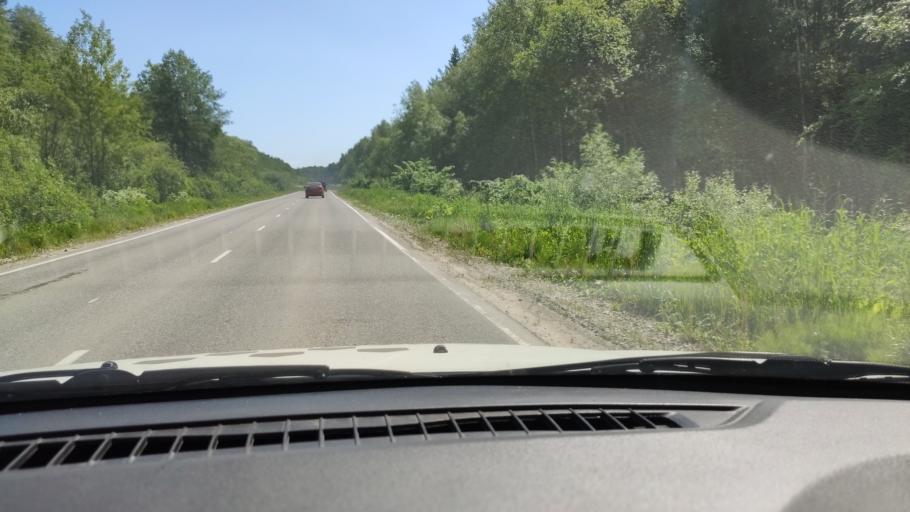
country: RU
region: Perm
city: Novyye Lyady
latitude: 58.0248
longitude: 56.6359
